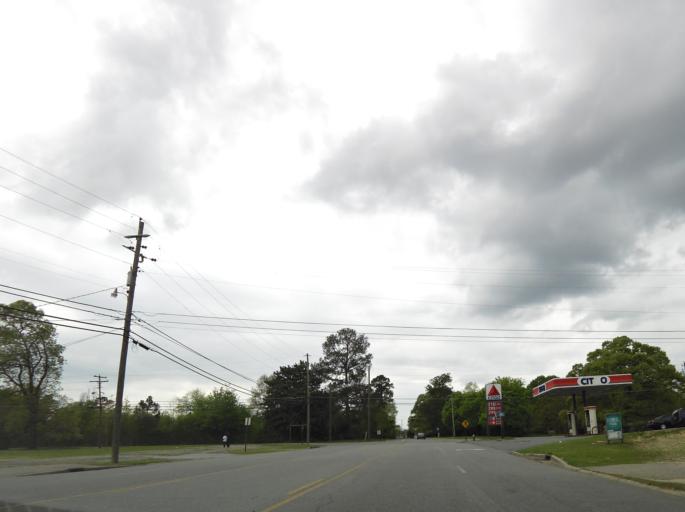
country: US
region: Georgia
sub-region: Houston County
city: Warner Robins
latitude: 32.6131
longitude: -83.6001
